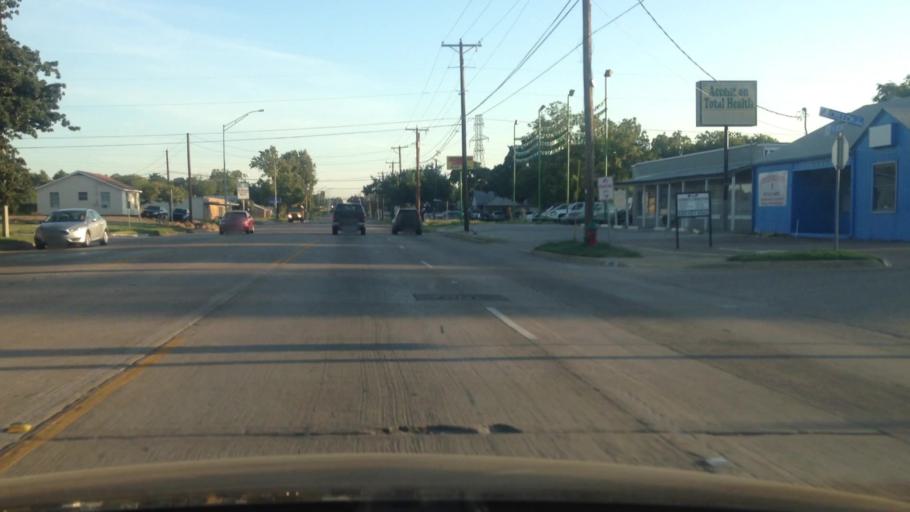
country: US
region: Texas
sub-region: Tarrant County
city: Haltom City
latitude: 32.7890
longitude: -97.2906
